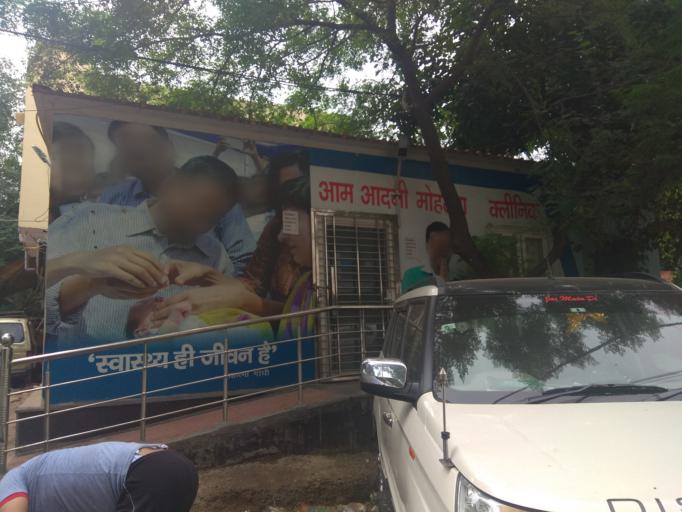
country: IN
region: NCT
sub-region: New Delhi
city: New Delhi
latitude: 28.5710
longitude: 77.2547
